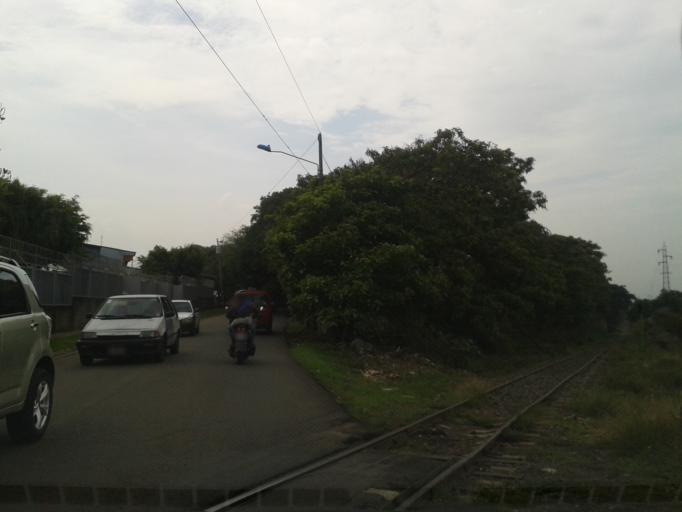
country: CR
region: Heredia
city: San Pablo
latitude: 9.9858
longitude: -84.1078
